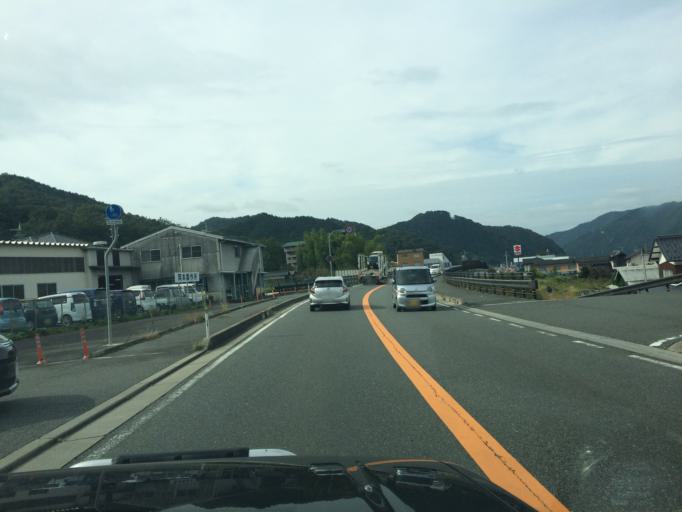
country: JP
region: Hyogo
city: Toyooka
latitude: 35.3398
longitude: 134.8441
